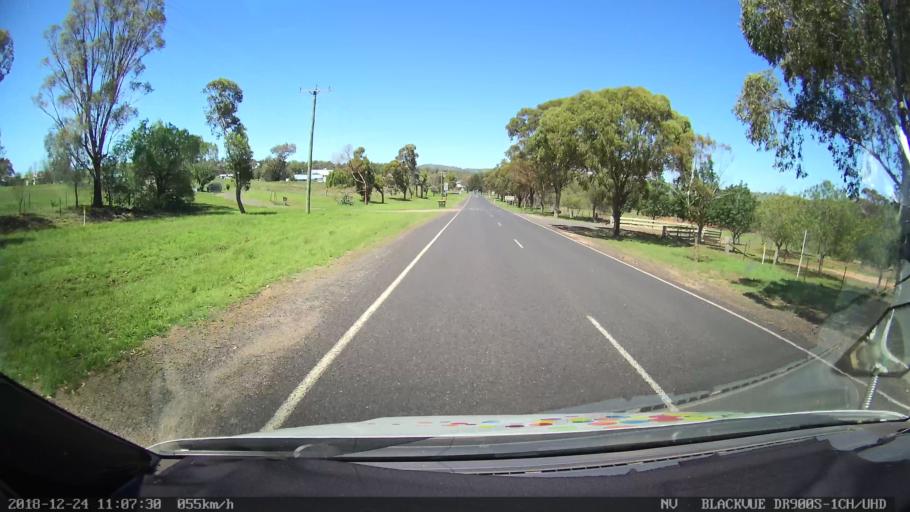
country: AU
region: New South Wales
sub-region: Upper Hunter Shire
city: Merriwa
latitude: -32.1335
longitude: 150.3594
